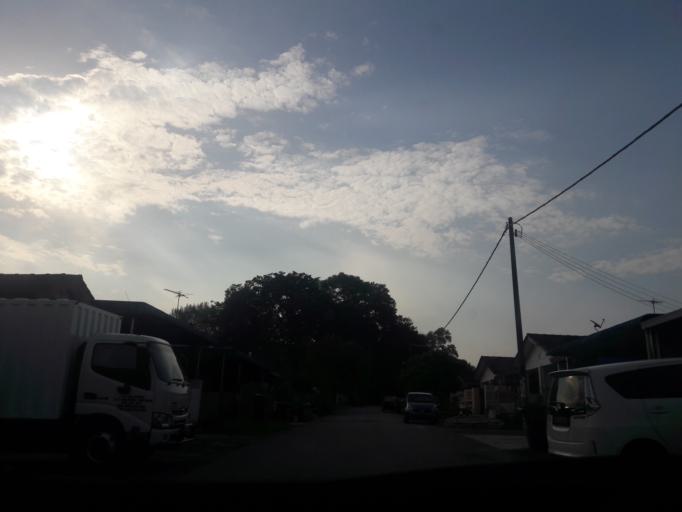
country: MY
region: Kedah
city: Kulim
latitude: 5.3735
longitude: 100.5326
